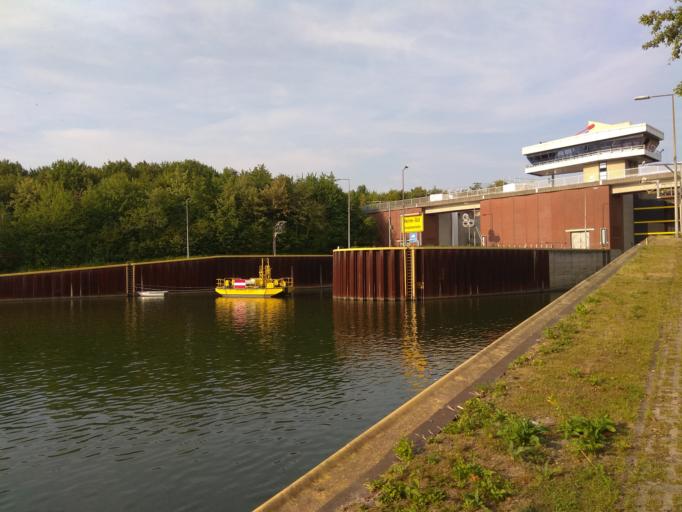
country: DE
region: North Rhine-Westphalia
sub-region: Regierungsbezirk Arnsberg
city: Herne
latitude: 51.5638
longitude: 7.2398
